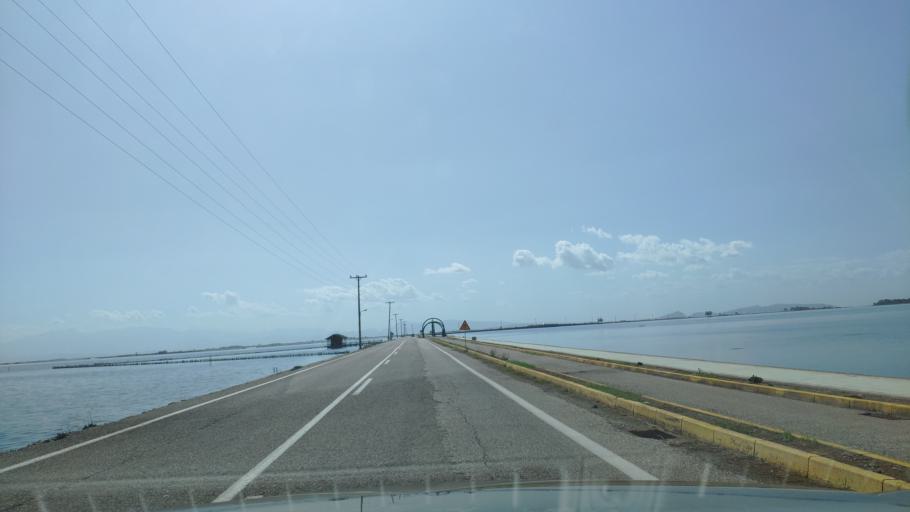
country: GR
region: West Greece
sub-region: Nomos Aitolias kai Akarnanias
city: Mesolongi
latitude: 38.3582
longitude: 21.4274
